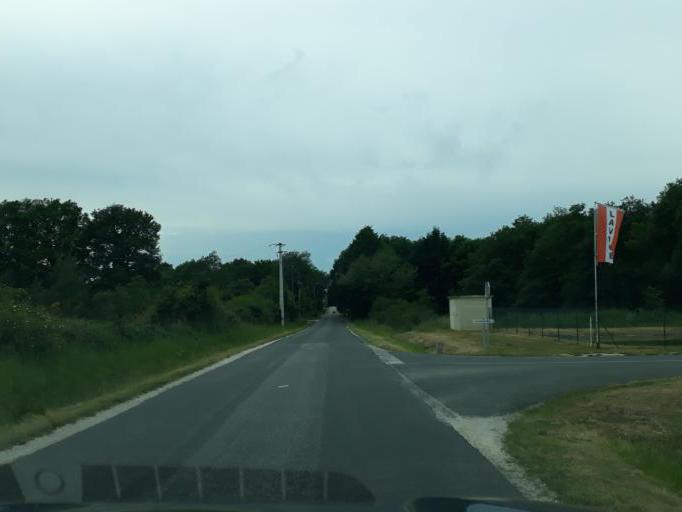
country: FR
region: Centre
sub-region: Departement du Loiret
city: Saint-Pere-sur-Loire
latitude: 47.7262
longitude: 2.3131
